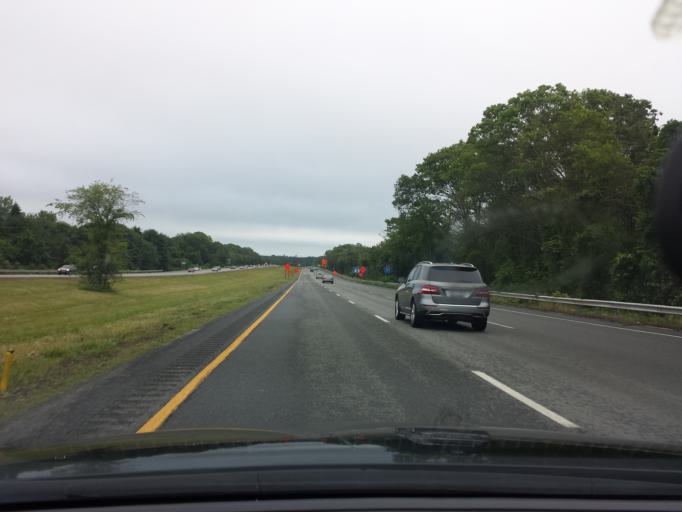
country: US
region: Massachusetts
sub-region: Bristol County
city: Ocean Grove
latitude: 41.7461
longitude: -71.2146
